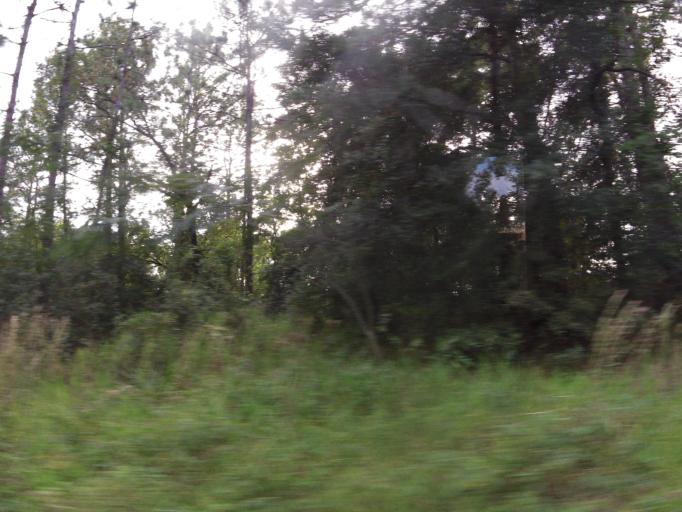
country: US
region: Florida
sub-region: Duval County
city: Jacksonville
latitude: 30.4277
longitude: -81.6511
